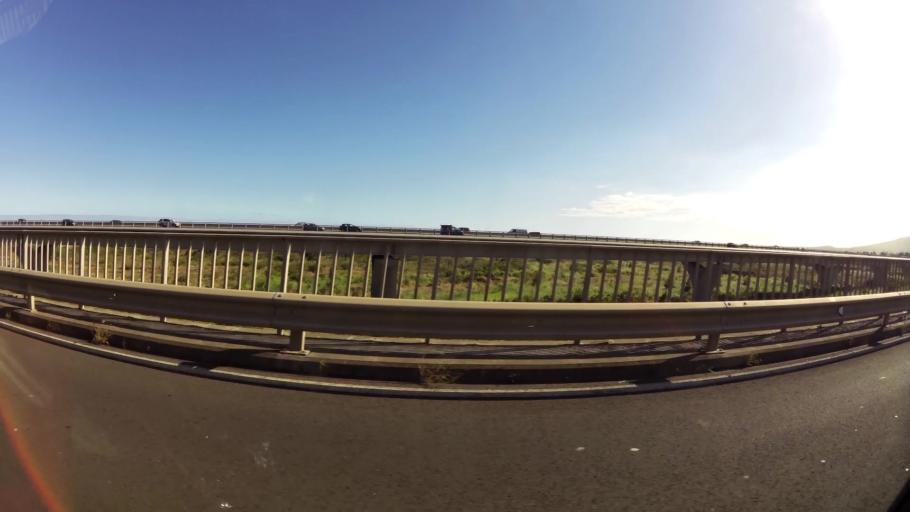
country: RE
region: Reunion
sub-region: Reunion
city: Saint-Louis
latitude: -21.2951
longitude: 55.4170
